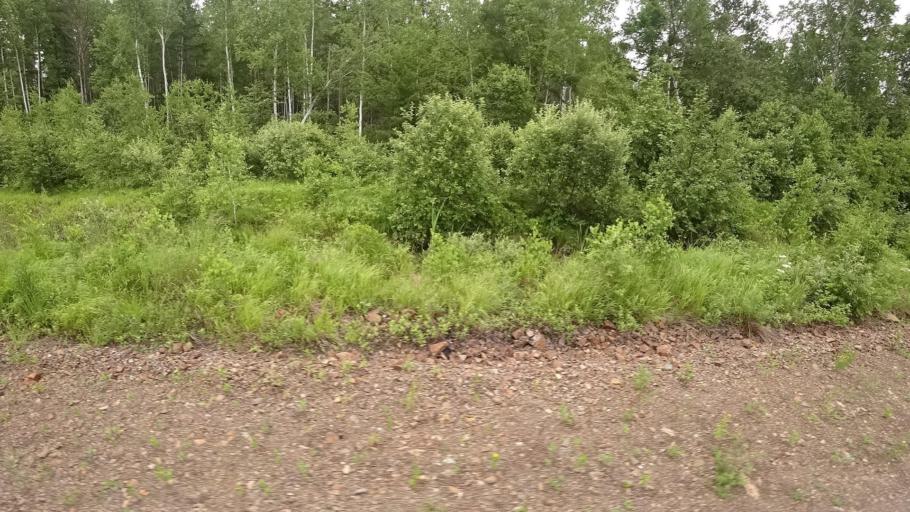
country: RU
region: Khabarovsk Krai
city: Amursk
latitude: 49.8972
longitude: 136.1651
